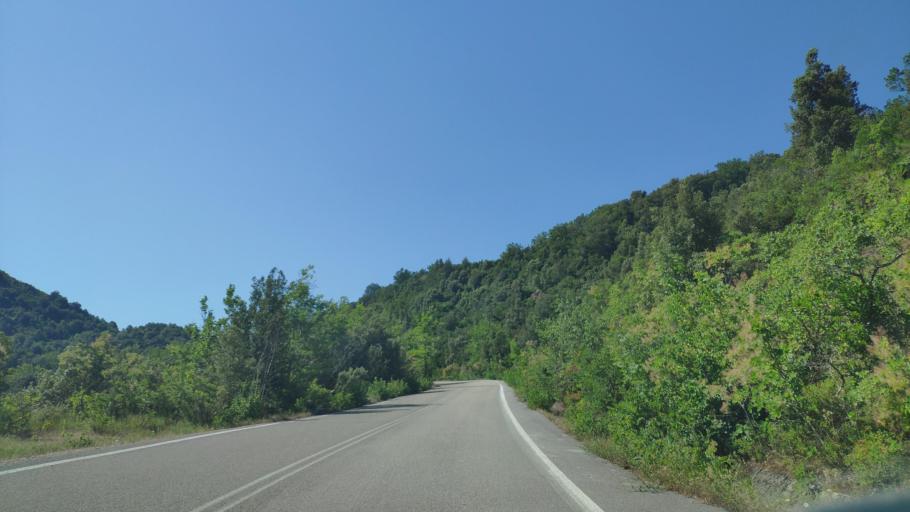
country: GR
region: West Greece
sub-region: Nomos Aitolias kai Akarnanias
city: Sardinia
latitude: 38.9238
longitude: 21.3910
